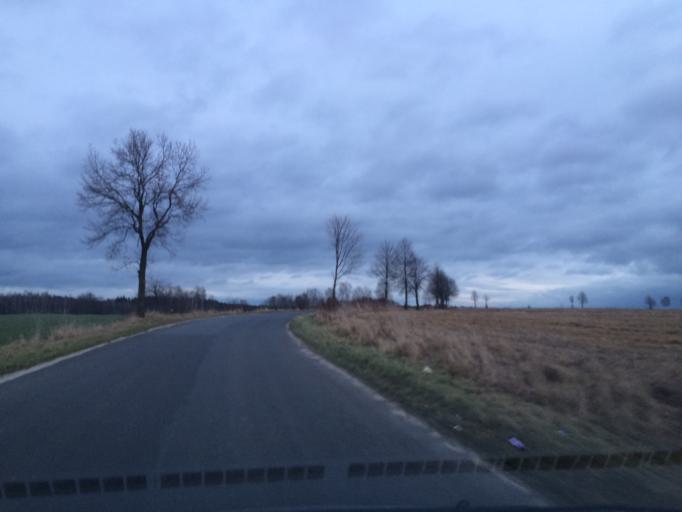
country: PL
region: Lower Silesian Voivodeship
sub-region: Powiat boleslawiecki
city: Nowogrodziec
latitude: 51.2020
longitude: 15.4208
